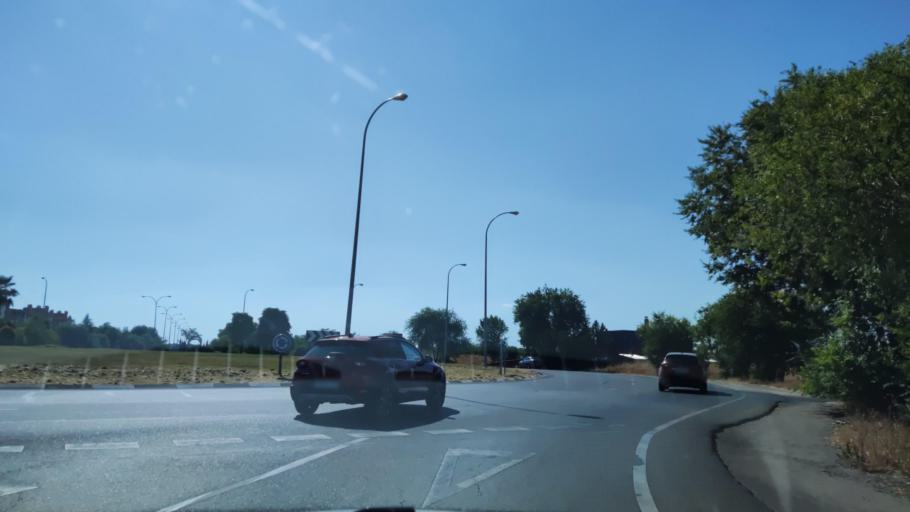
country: ES
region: Madrid
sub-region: Provincia de Madrid
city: Leganes
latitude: 40.3473
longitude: -3.7475
